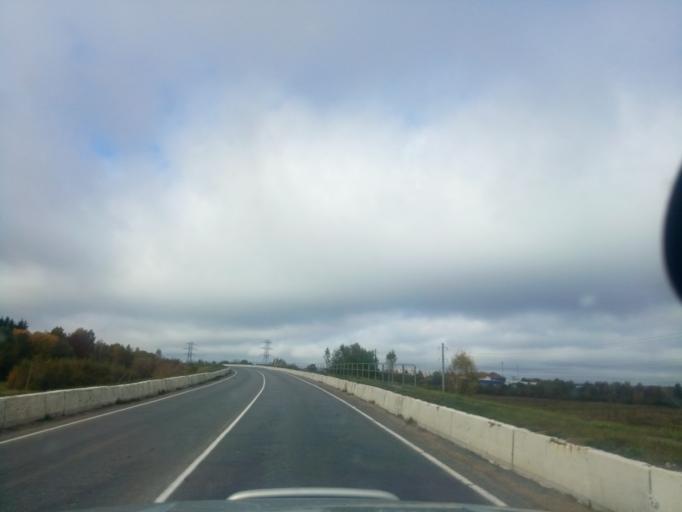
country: BY
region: Minsk
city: Zaslawye
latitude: 53.9978
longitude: 27.2876
